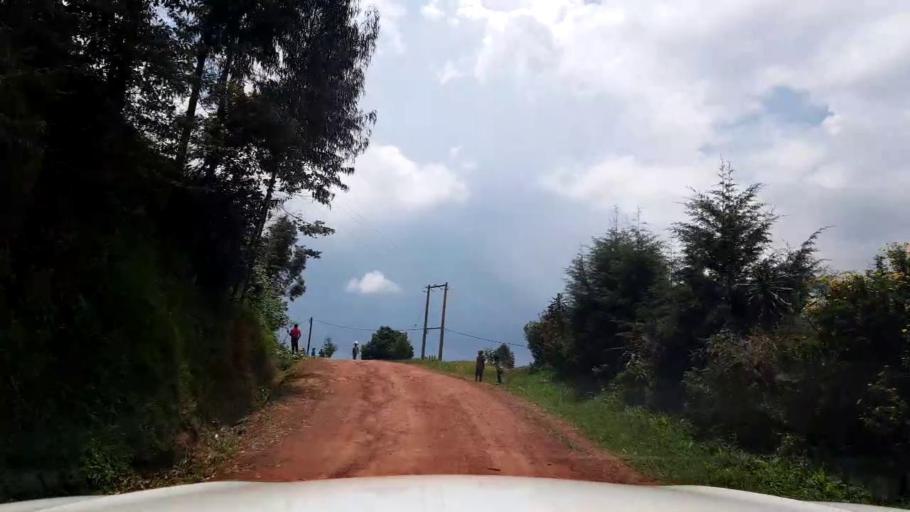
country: RW
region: Northern Province
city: Byumba
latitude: -1.4858
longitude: 29.9248
